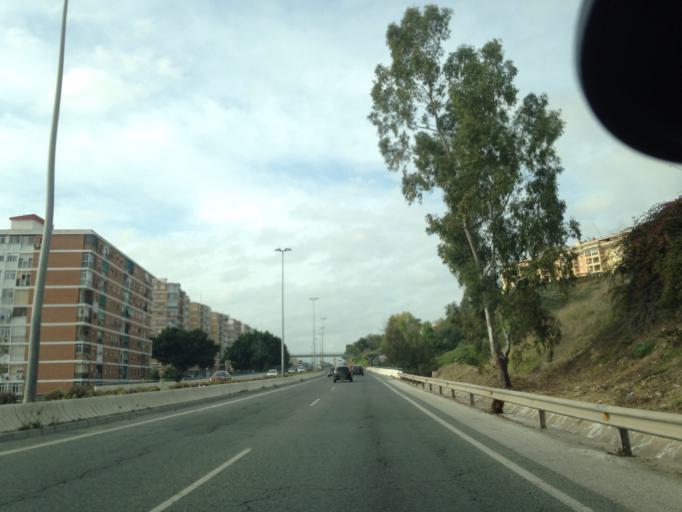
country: ES
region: Andalusia
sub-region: Provincia de Malaga
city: Malaga
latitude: 36.7328
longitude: -4.4400
